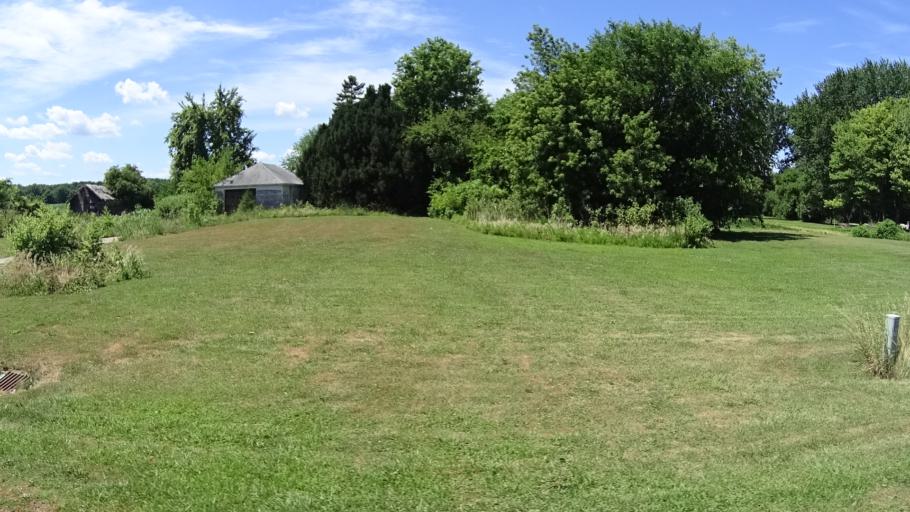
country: US
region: Ohio
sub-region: Erie County
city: Sandusky
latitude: 41.4026
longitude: -82.6790
